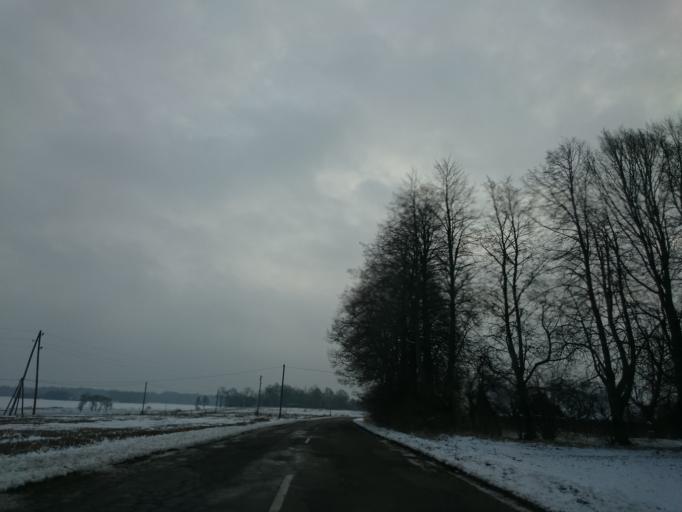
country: LV
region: Seja
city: Loja
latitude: 57.2339
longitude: 24.5539
